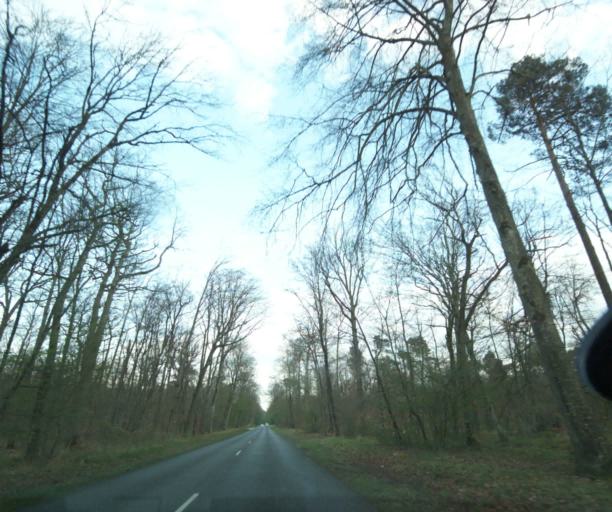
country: FR
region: Ile-de-France
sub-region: Departement de Seine-et-Marne
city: Fontainebleau
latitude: 48.3938
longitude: 2.7007
